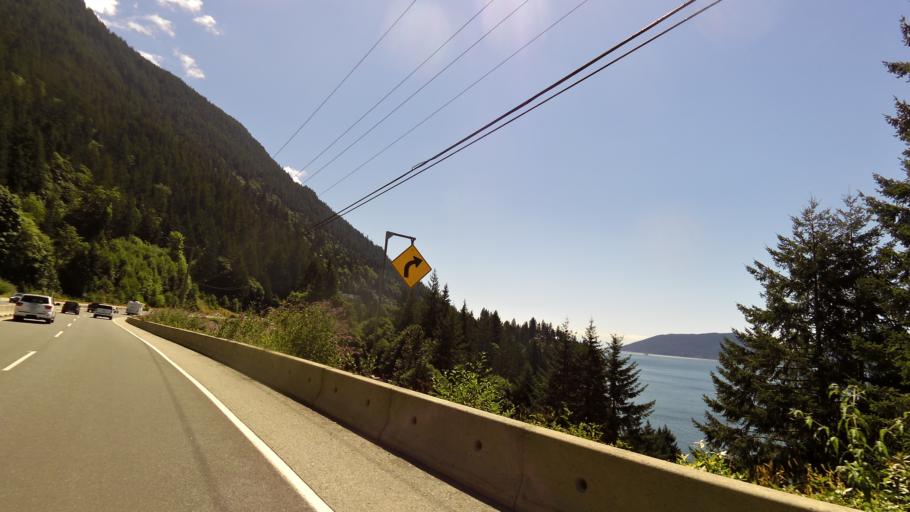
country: CA
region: British Columbia
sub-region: Greater Vancouver Regional District
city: Lions Bay
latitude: 49.4054
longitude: -123.2424
